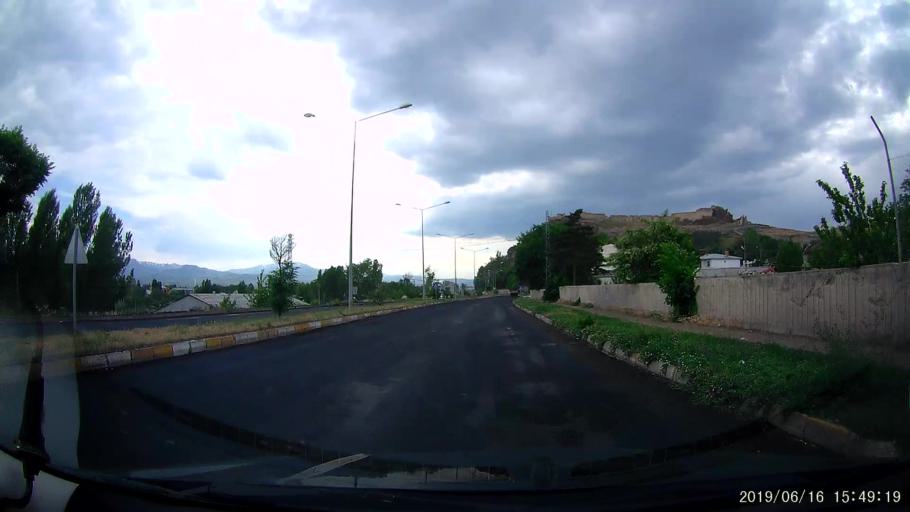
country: TR
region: Erzurum
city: Pasinler
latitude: 39.9788
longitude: 41.6882
